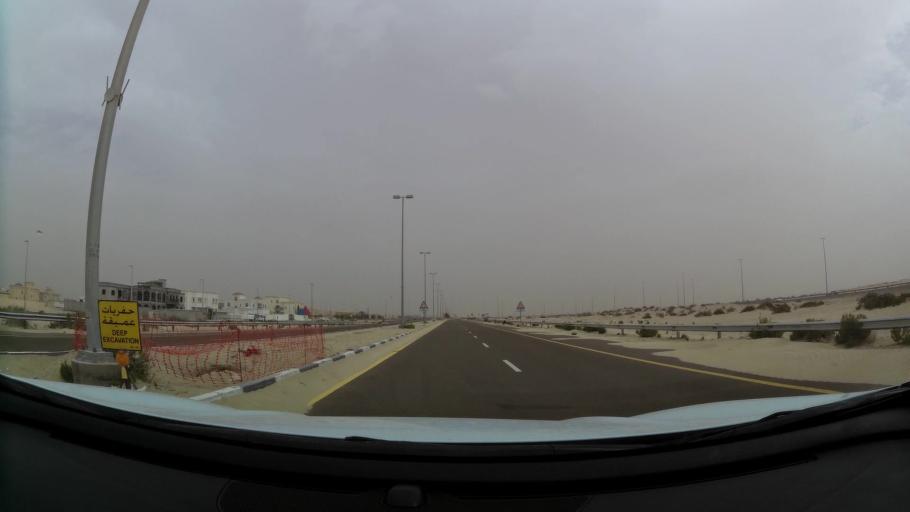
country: AE
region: Abu Dhabi
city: Abu Dhabi
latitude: 24.3585
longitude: 54.7150
